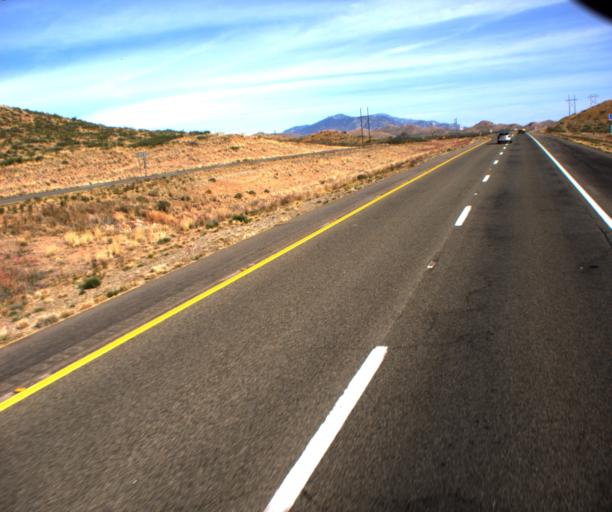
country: US
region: Arizona
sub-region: Cochise County
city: Willcox
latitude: 32.4626
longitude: -109.6682
